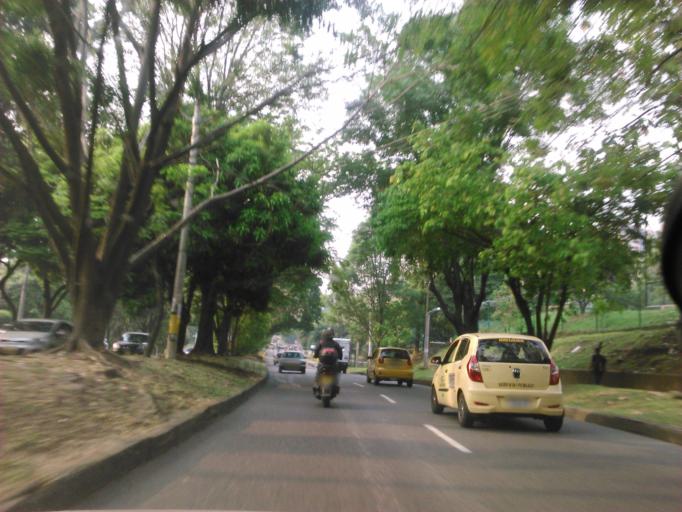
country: CO
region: Antioquia
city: Itagui
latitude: 6.2232
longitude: -75.5995
